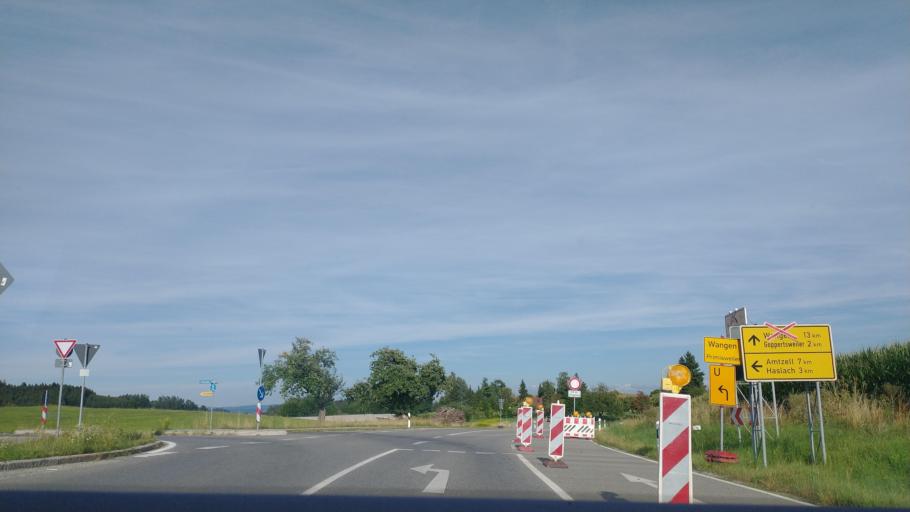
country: DE
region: Baden-Wuerttemberg
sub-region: Tuebingen Region
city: Neukirch
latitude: 47.6599
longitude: 9.7131
